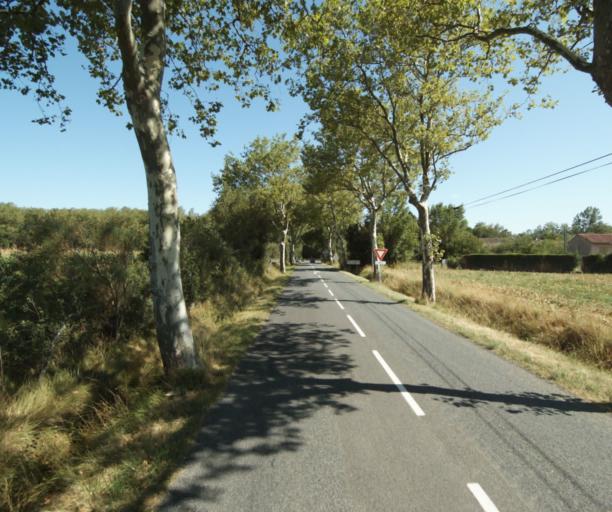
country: FR
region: Midi-Pyrenees
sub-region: Departement du Tarn
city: Soreze
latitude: 43.4496
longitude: 2.0458
